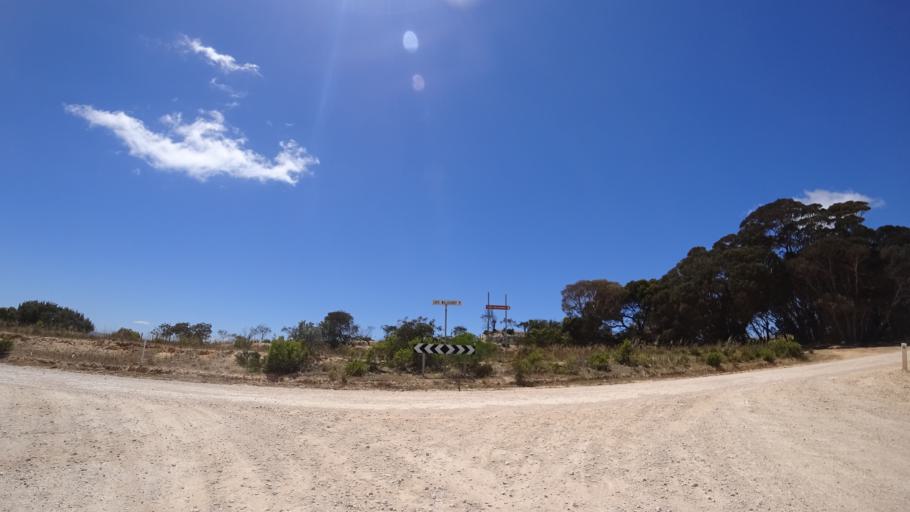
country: AU
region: South Australia
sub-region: Yankalilla
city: Normanville
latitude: -35.8111
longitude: 138.0724
